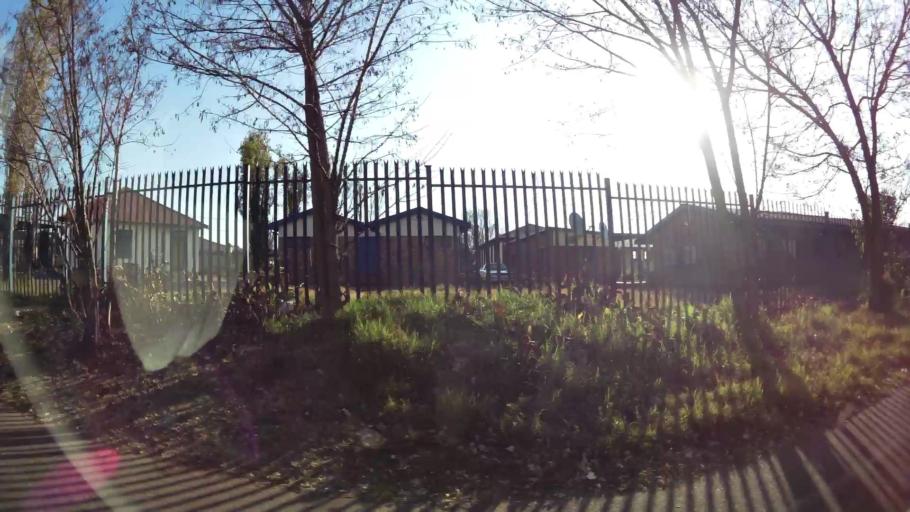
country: ZA
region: Gauteng
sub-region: City of Johannesburg Metropolitan Municipality
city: Soweto
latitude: -26.2662
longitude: 27.8751
